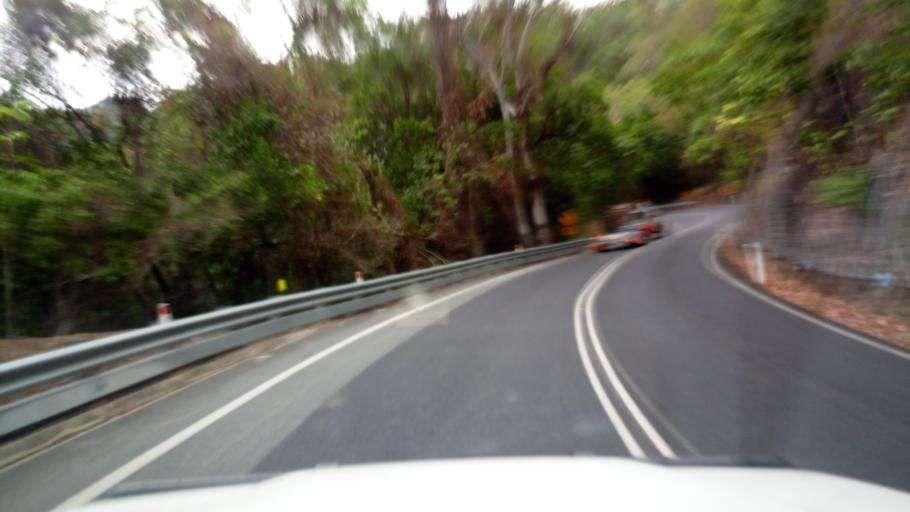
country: AU
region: Queensland
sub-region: Cairns
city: Redlynch
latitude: -16.8391
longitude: 145.6845
